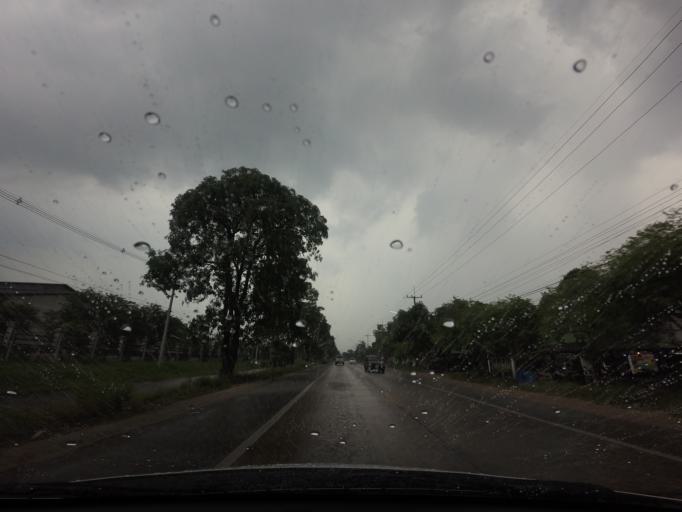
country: TH
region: Nakhon Pathom
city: Sam Phran
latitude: 13.7750
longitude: 100.2319
